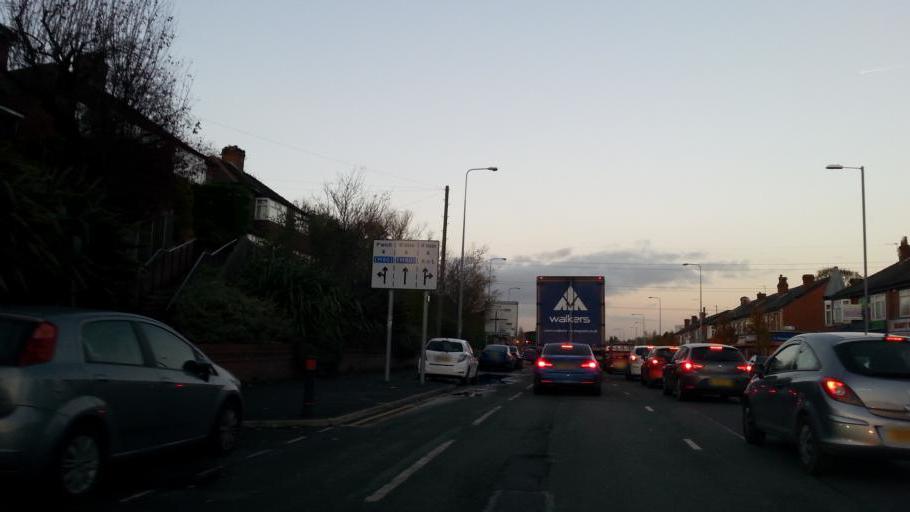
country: GB
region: England
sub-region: Manchester
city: Blackley
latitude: 53.5311
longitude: -2.2093
